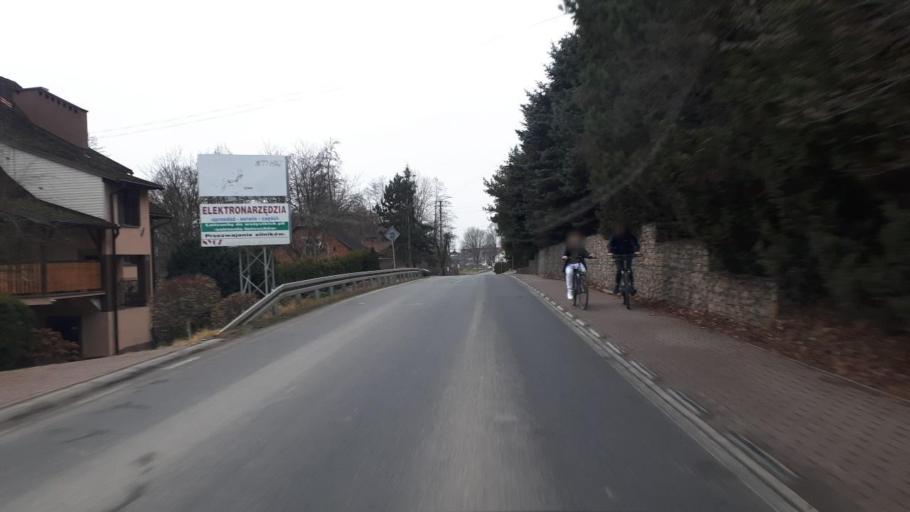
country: PL
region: Silesian Voivodeship
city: Janowice
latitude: 49.9045
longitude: 19.1175
